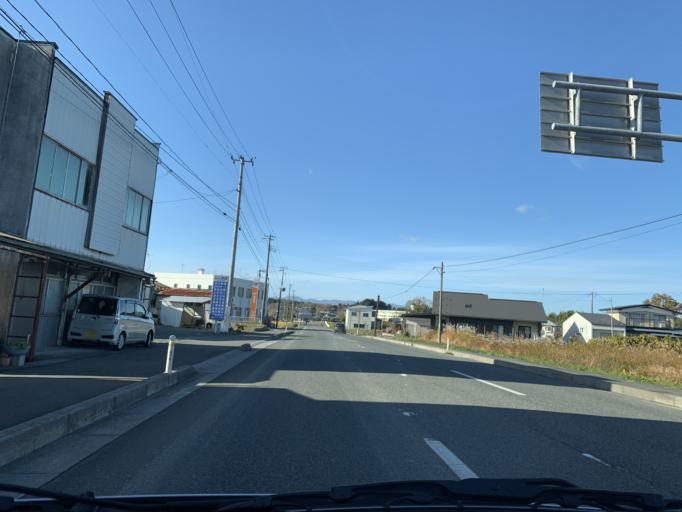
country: JP
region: Iwate
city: Mizusawa
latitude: 39.2031
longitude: 141.1146
